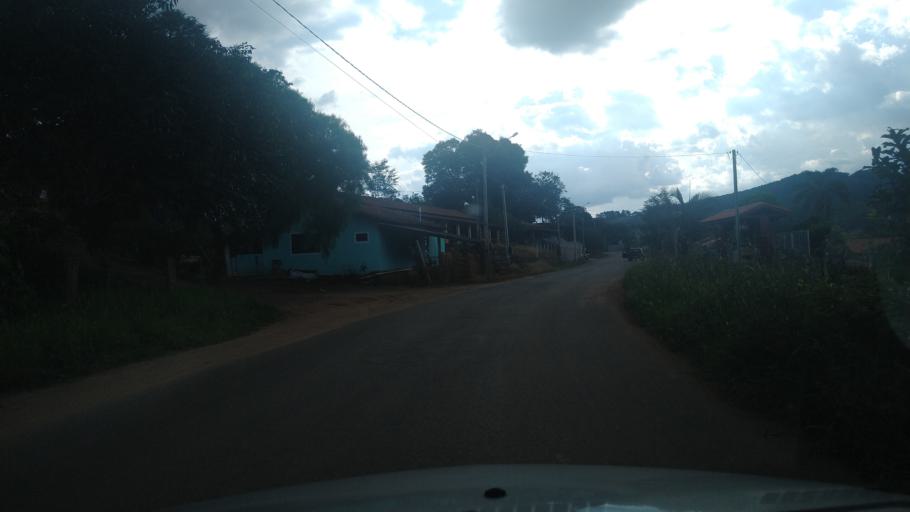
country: BR
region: Minas Gerais
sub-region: Extrema
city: Extrema
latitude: -22.7223
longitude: -46.3450
